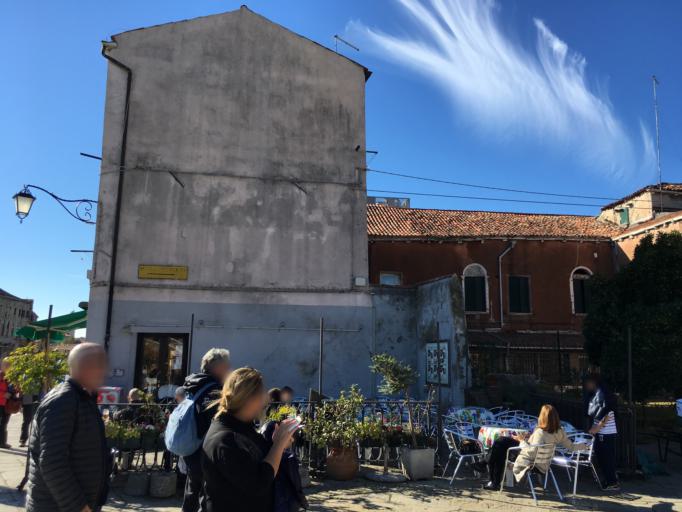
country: IT
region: Veneto
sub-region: Provincia di Venezia
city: Murano
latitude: 45.4570
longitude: 12.3574
